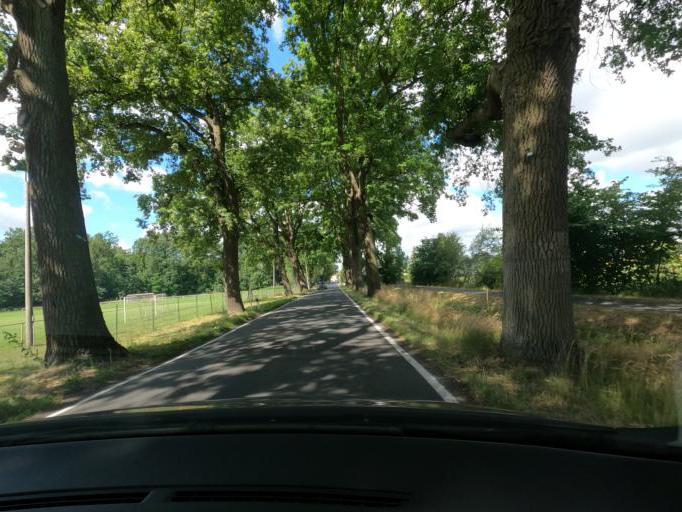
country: DE
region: Brandenburg
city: Kremmen
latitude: 52.7287
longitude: 12.9629
